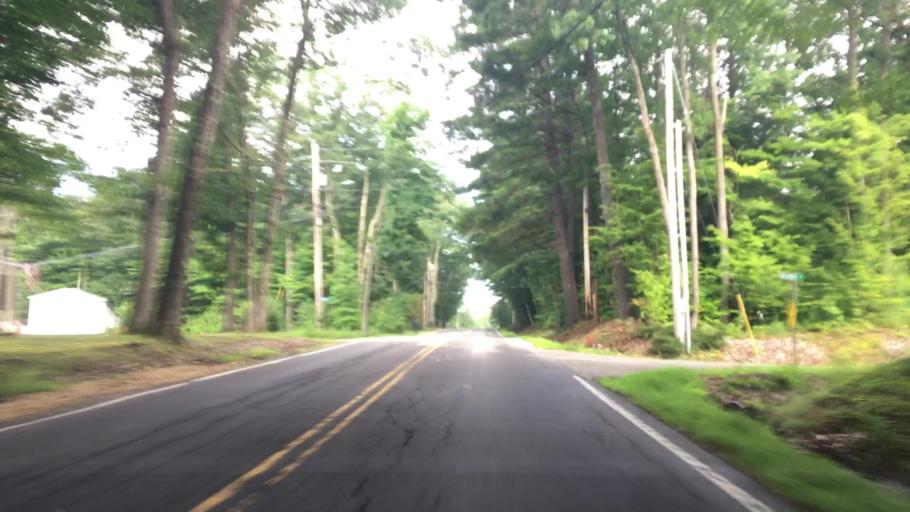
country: US
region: New Hampshire
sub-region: Strafford County
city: Rochester
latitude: 43.3581
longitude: -70.9929
